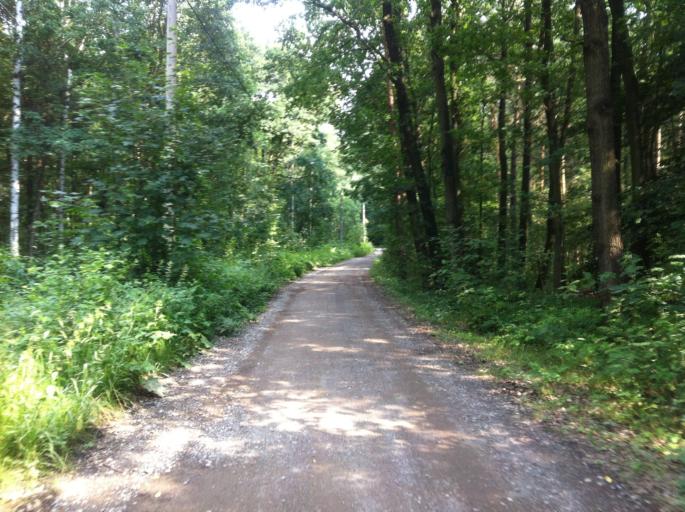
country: DE
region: Saxony
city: Machern
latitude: 51.3197
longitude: 12.6683
